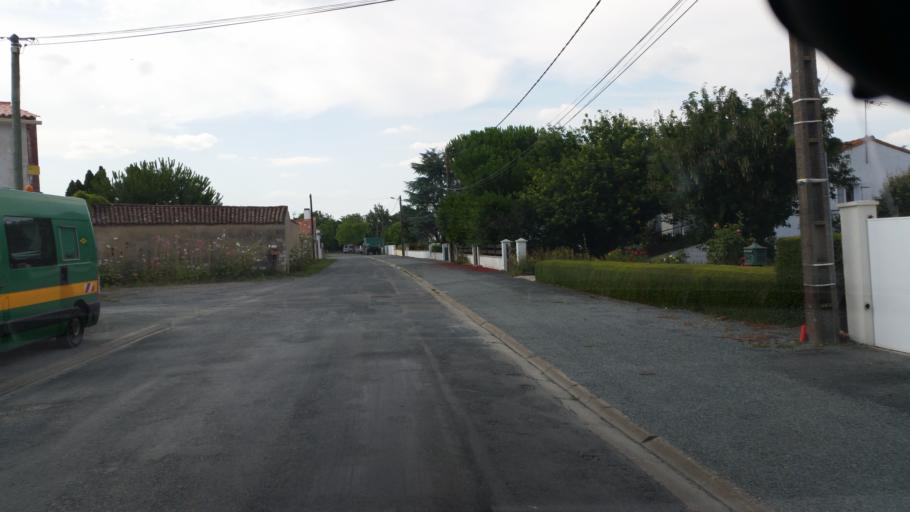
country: FR
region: Poitou-Charentes
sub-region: Departement de la Charente-Maritime
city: Marans
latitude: 46.3062
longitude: -0.9839
